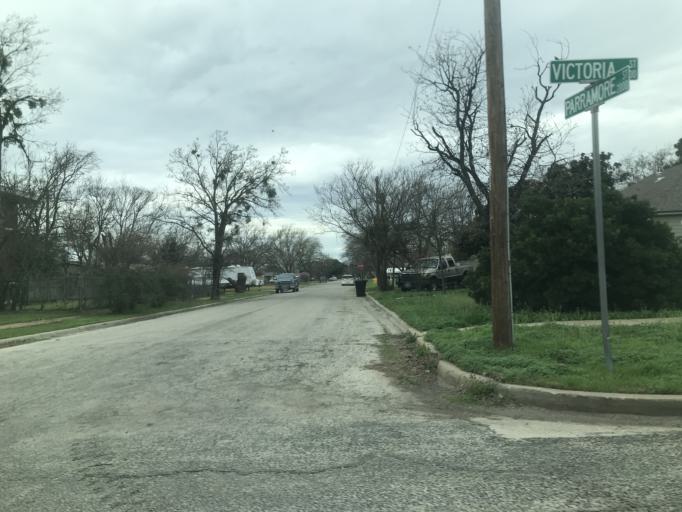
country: US
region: Texas
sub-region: Taylor County
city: Abilene
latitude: 32.4569
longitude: -99.7455
